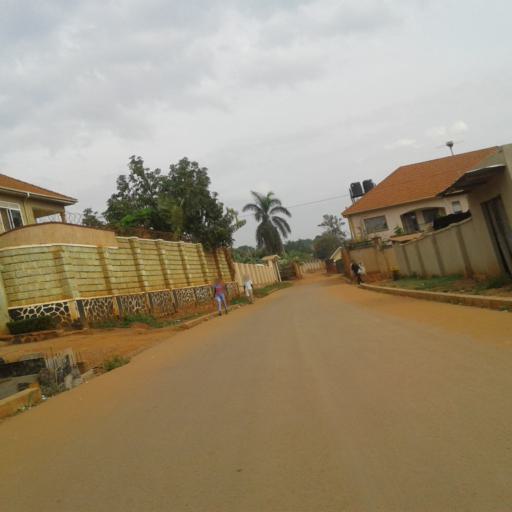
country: UG
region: Central Region
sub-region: Kampala District
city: Kampala
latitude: 0.2681
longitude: 32.6268
